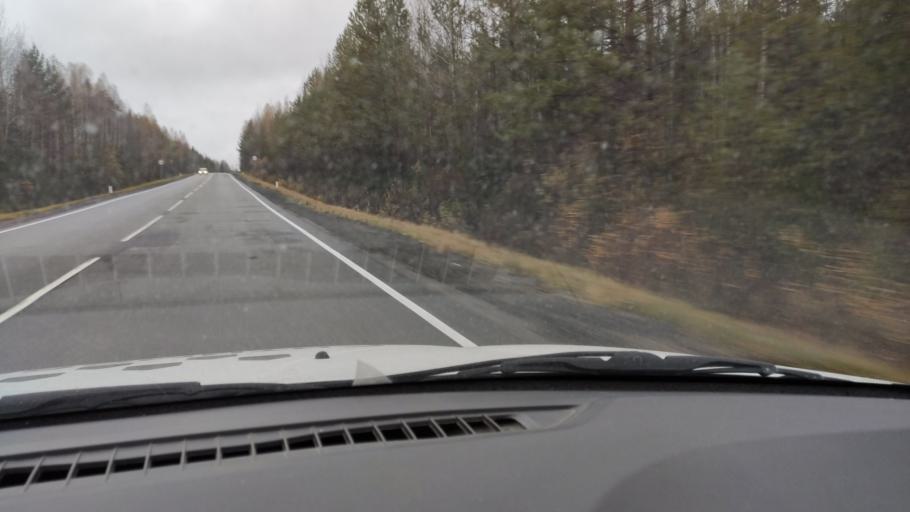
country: RU
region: Kirov
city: Chernaya Kholunitsa
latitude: 58.8648
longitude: 51.5829
